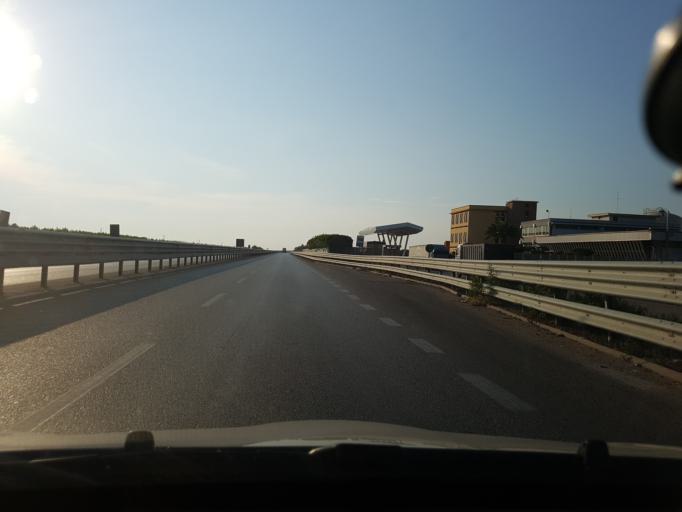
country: IT
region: Apulia
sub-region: Provincia di Foggia
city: Stornara
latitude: 41.3012
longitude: 15.8172
